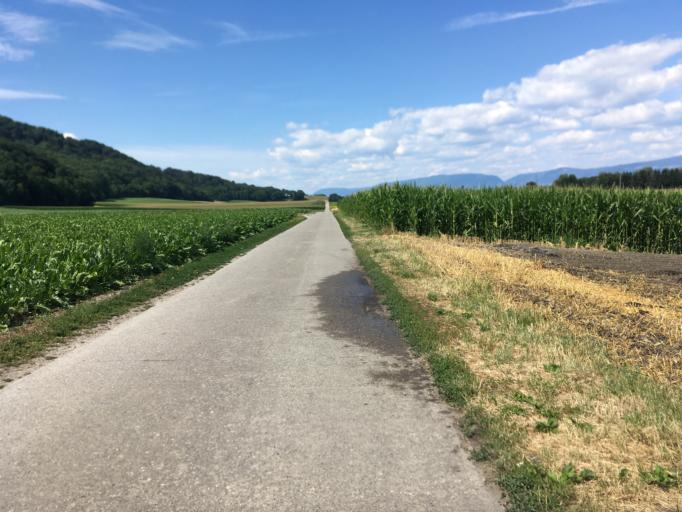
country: CH
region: Fribourg
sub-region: See District
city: Bas-Vully
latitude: 46.9701
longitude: 7.0877
